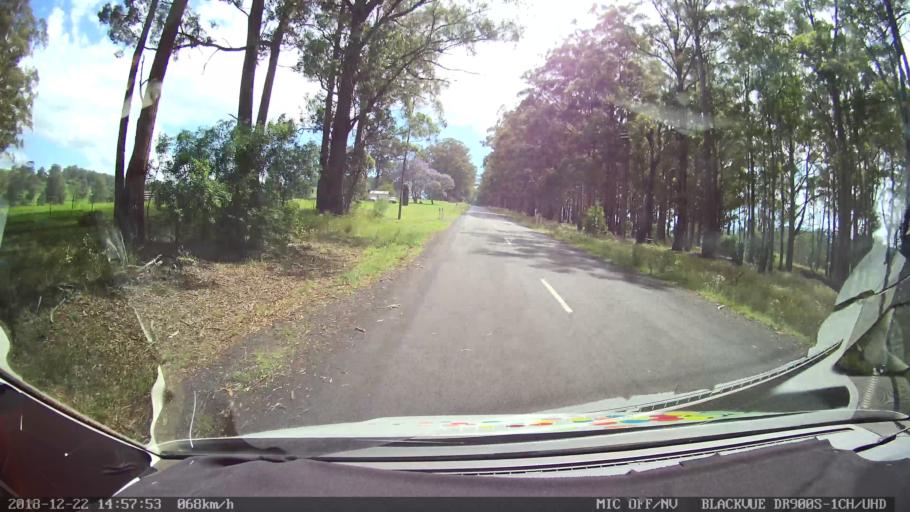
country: AU
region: New South Wales
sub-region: Bellingen
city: Dorrigo
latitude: -30.2369
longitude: 152.4964
